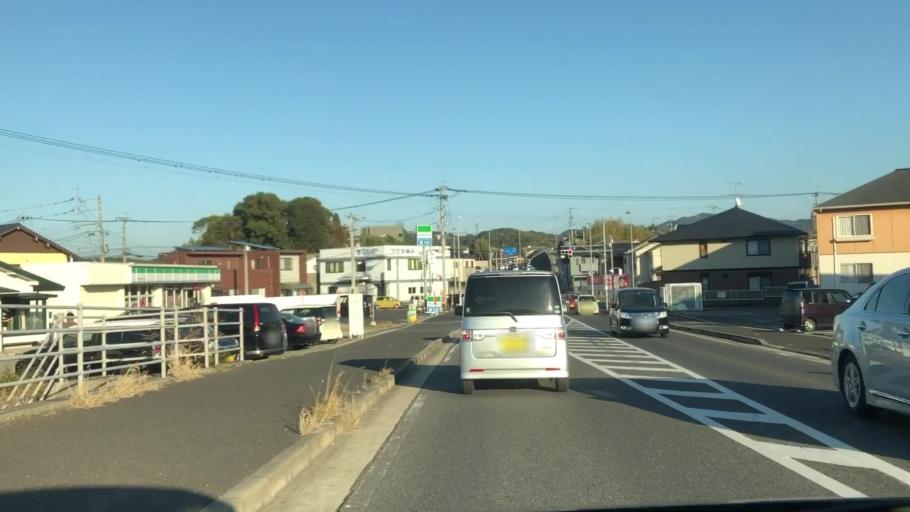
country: JP
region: Nagasaki
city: Sasebo
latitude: 33.1270
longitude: 129.7951
